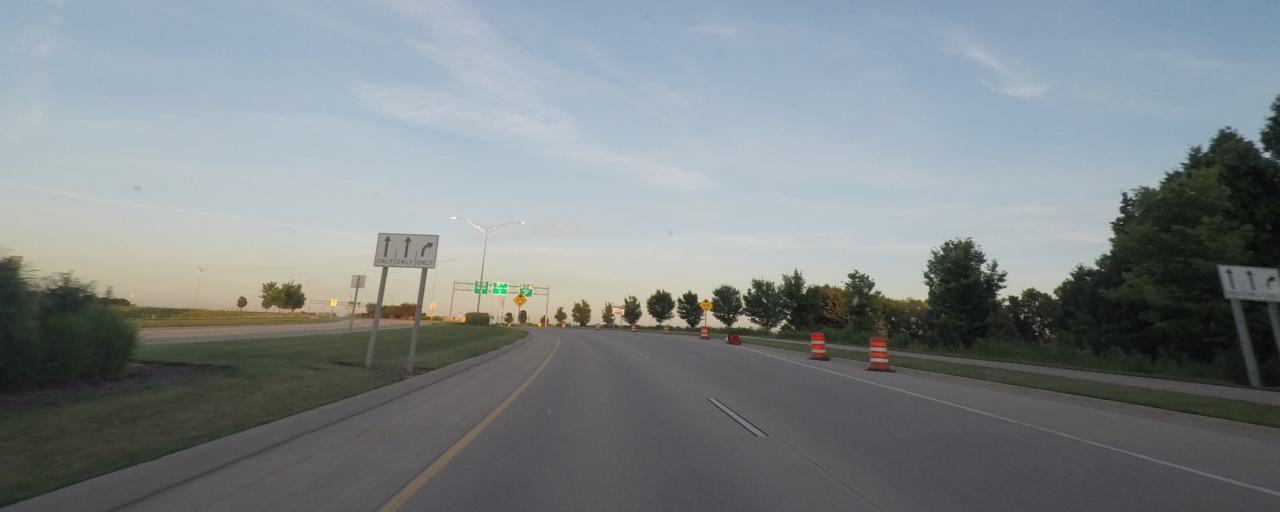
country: US
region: Wisconsin
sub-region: Rock County
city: Janesville
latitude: 42.6717
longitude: -88.9878
